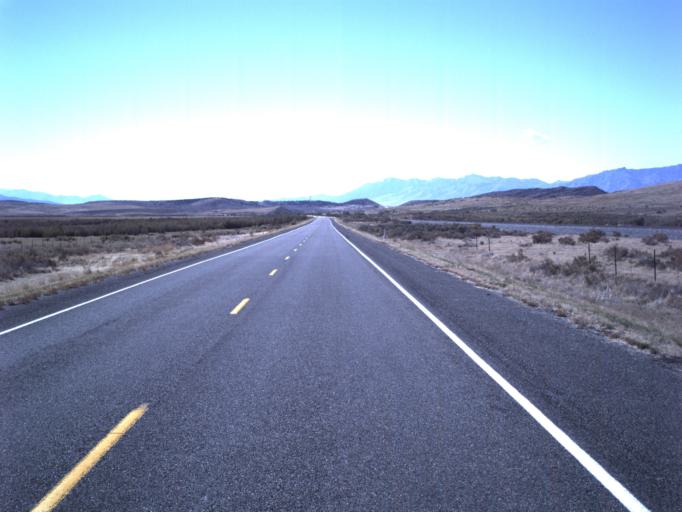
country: US
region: Utah
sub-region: Juab County
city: Nephi
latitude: 39.5028
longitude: -111.9558
